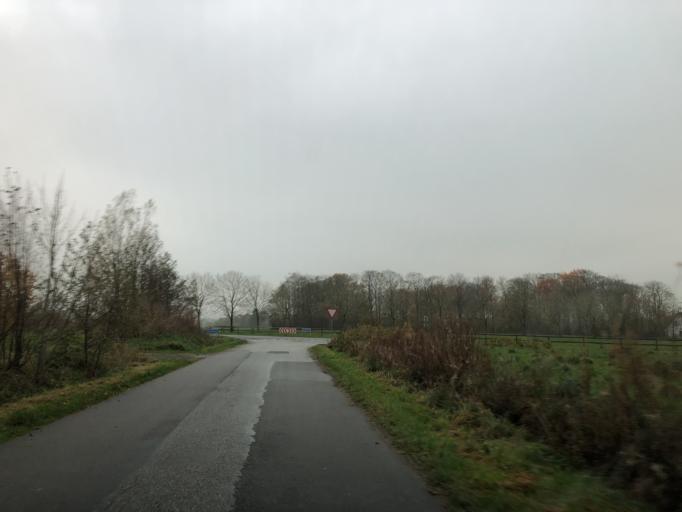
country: DK
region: Central Jutland
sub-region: Herning Kommune
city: Vildbjerg
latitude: 56.2084
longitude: 8.7572
